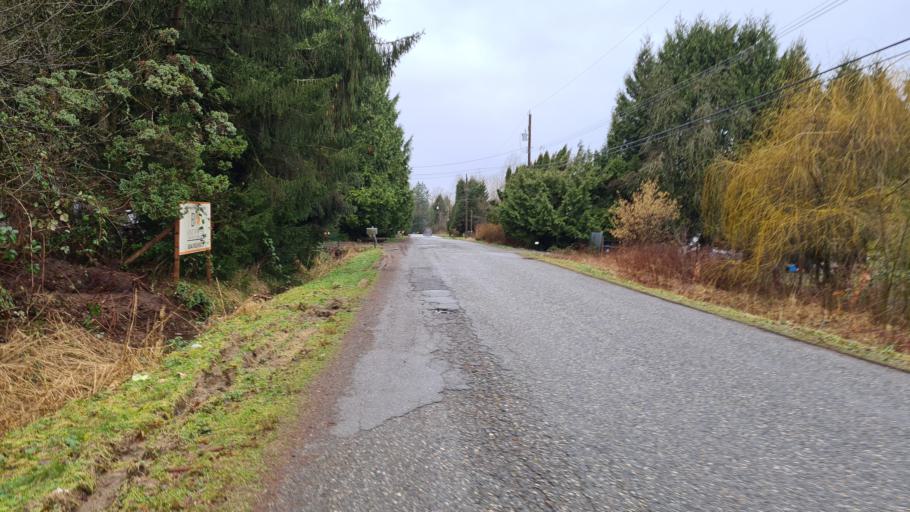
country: CA
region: British Columbia
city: Walnut Grove
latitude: 49.1383
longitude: -122.6553
